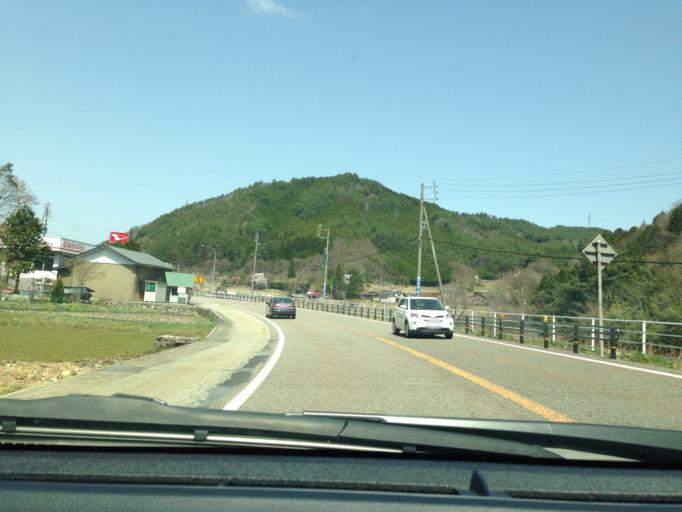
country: JP
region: Gifu
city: Takayama
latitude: 36.0345
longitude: 137.2906
